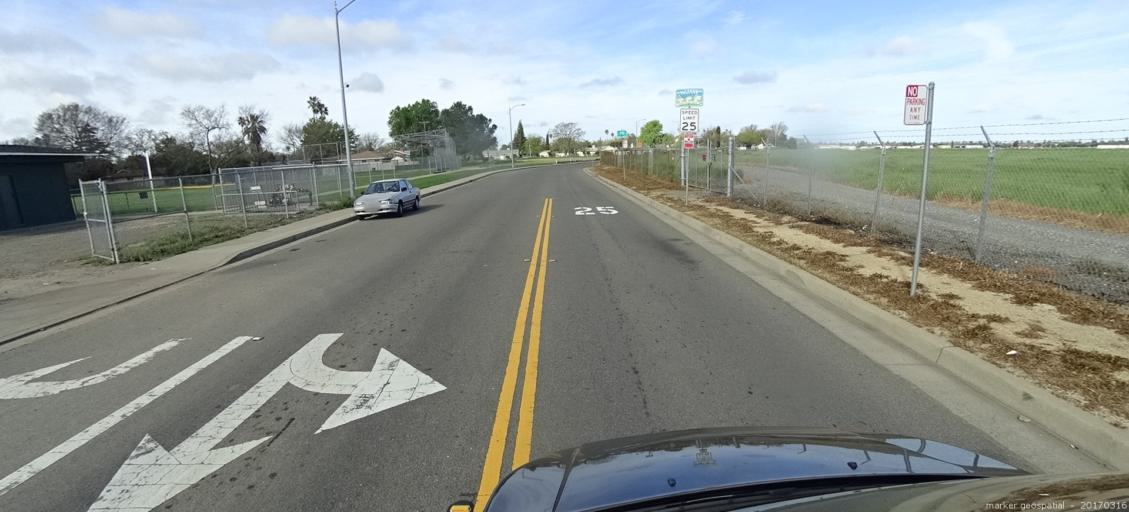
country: US
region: California
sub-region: Sacramento County
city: Parkway
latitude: 38.5092
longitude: -121.4833
